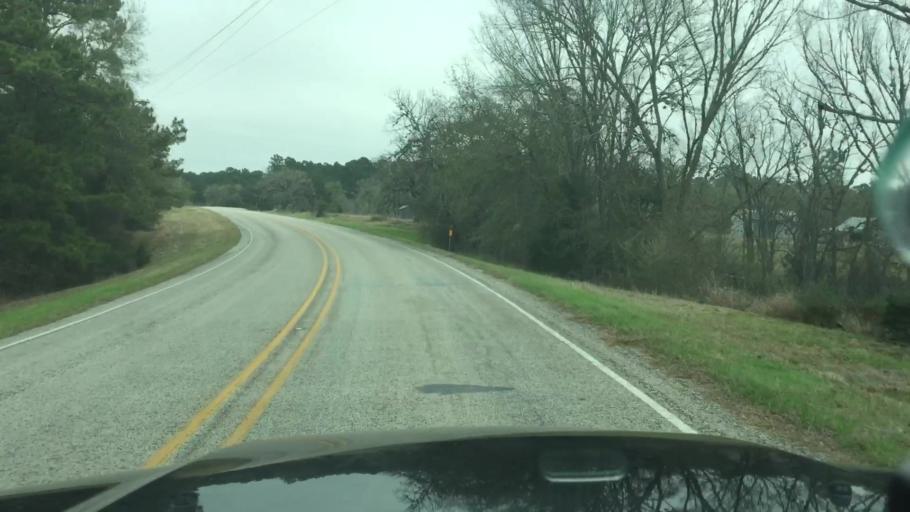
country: US
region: Texas
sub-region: Fayette County
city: La Grange
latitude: 30.0122
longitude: -96.9277
